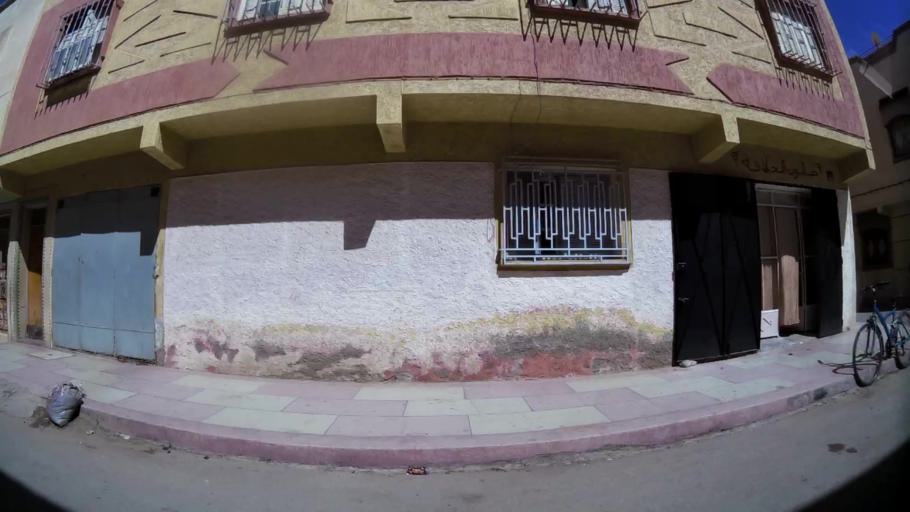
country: MA
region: Oriental
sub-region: Oujda-Angad
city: Oujda
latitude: 34.6841
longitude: -1.9355
